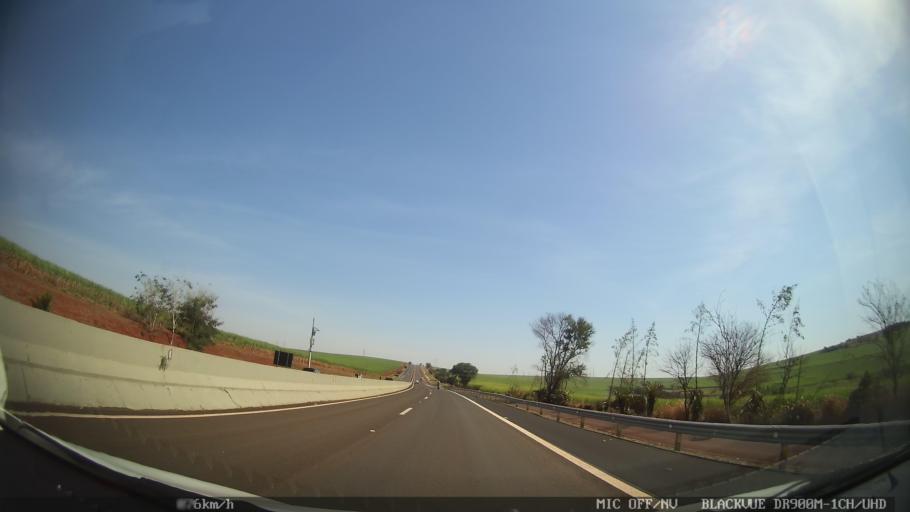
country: BR
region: Sao Paulo
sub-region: Ribeirao Preto
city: Ribeirao Preto
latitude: -21.1658
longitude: -47.8777
